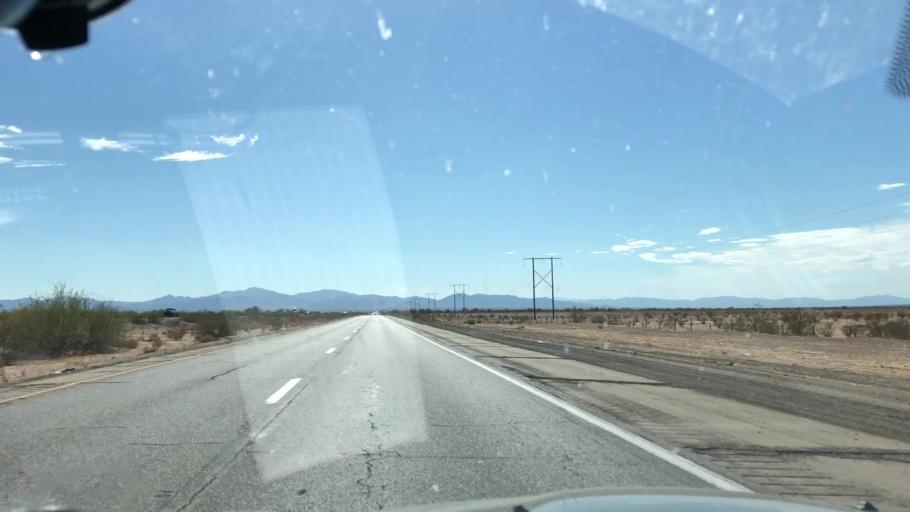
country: US
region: California
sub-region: Riverside County
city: Mesa Verde
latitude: 33.6062
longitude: -114.9587
